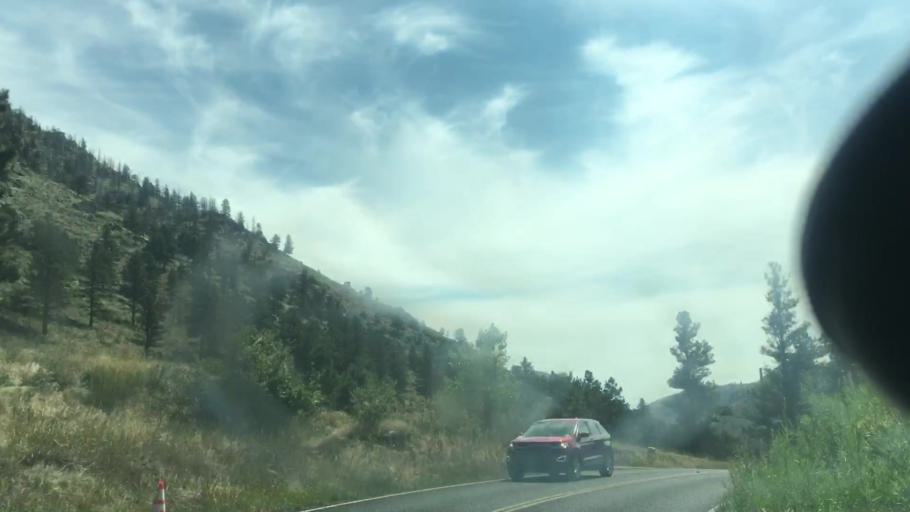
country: US
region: Colorado
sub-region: Larimer County
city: Laporte
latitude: 40.5783
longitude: -105.3302
